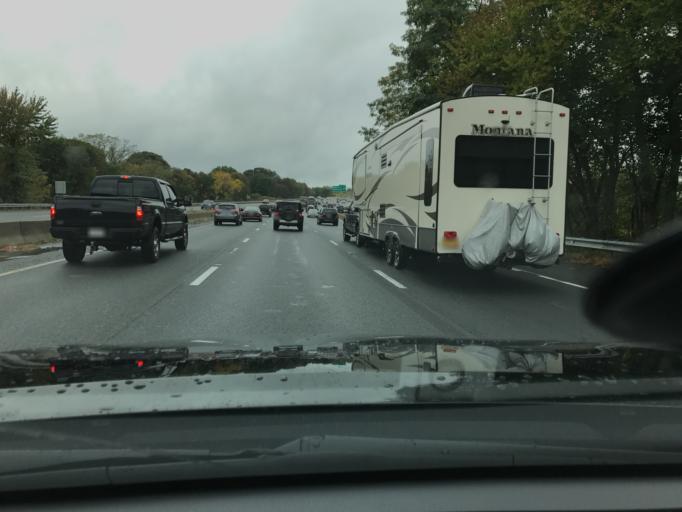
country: US
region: Massachusetts
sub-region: Essex County
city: Lynnfield
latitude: 42.5130
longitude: -71.0352
